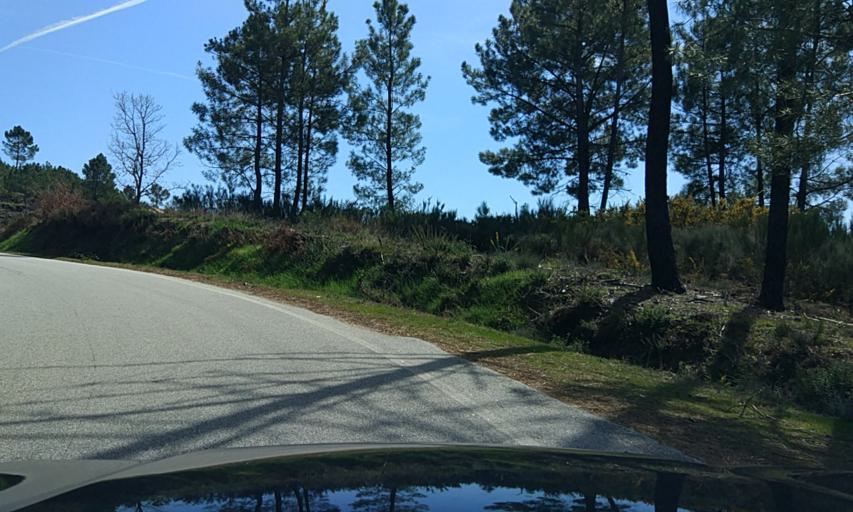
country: PT
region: Vila Real
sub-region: Sabrosa
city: Sabrosa
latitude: 41.3375
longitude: -7.5811
